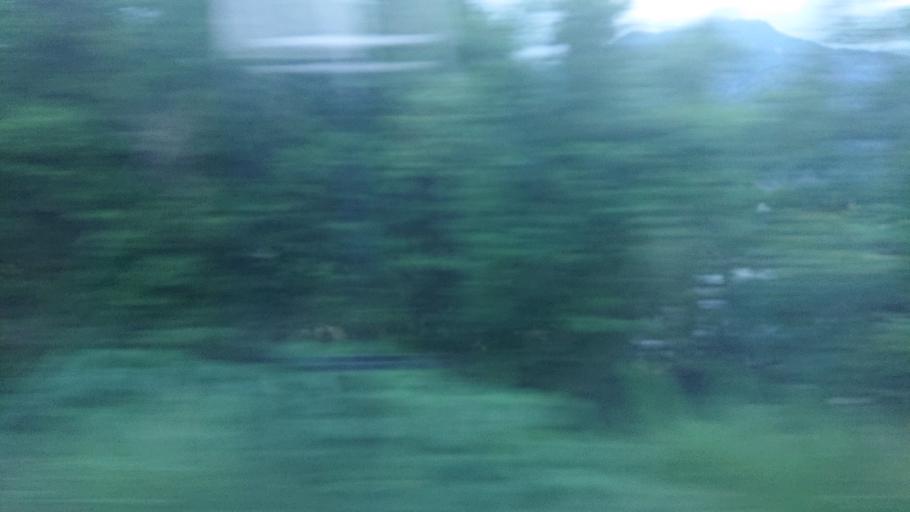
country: TW
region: Taiwan
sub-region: Taitung
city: Taitung
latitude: 23.0423
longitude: 121.1634
